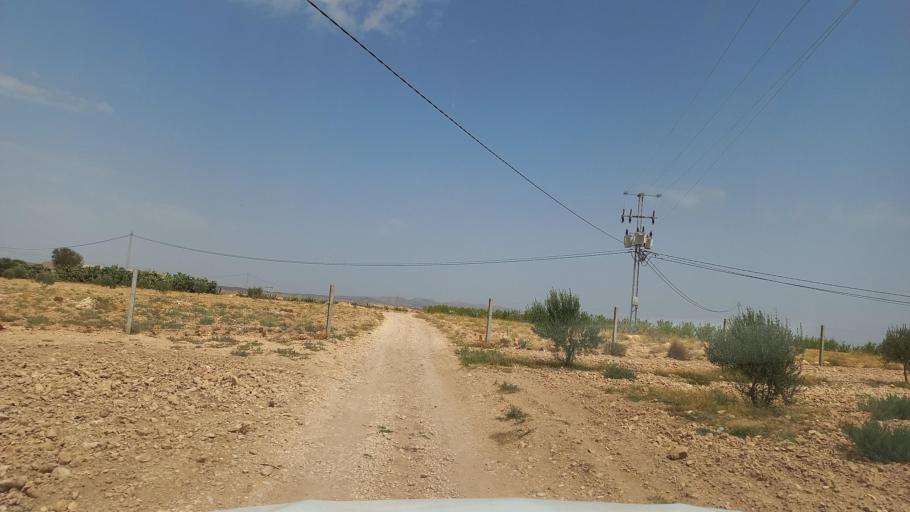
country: TN
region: Al Qasrayn
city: Kasserine
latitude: 35.2859
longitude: 9.0088
